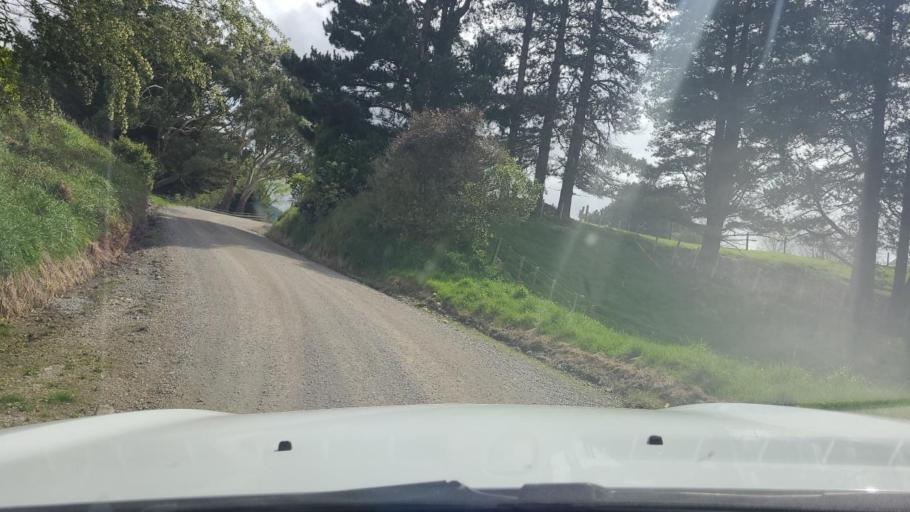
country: NZ
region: Wellington
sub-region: Masterton District
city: Masterton
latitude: -40.9524
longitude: 175.5291
